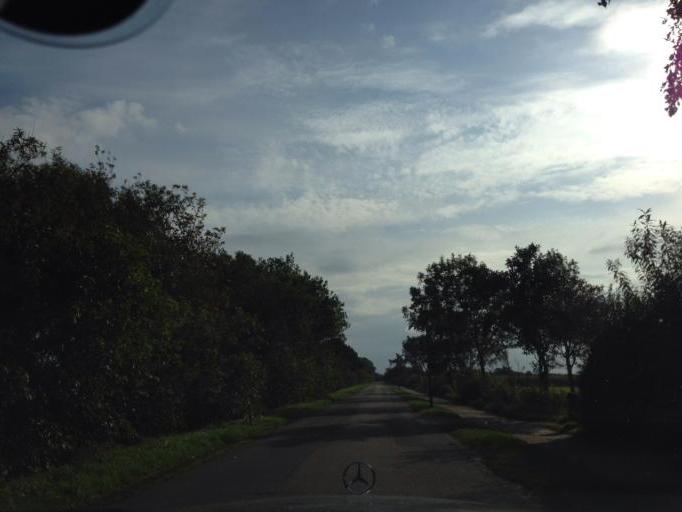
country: DE
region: Schleswig-Holstein
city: Nieblum
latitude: 54.6861
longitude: 8.4936
